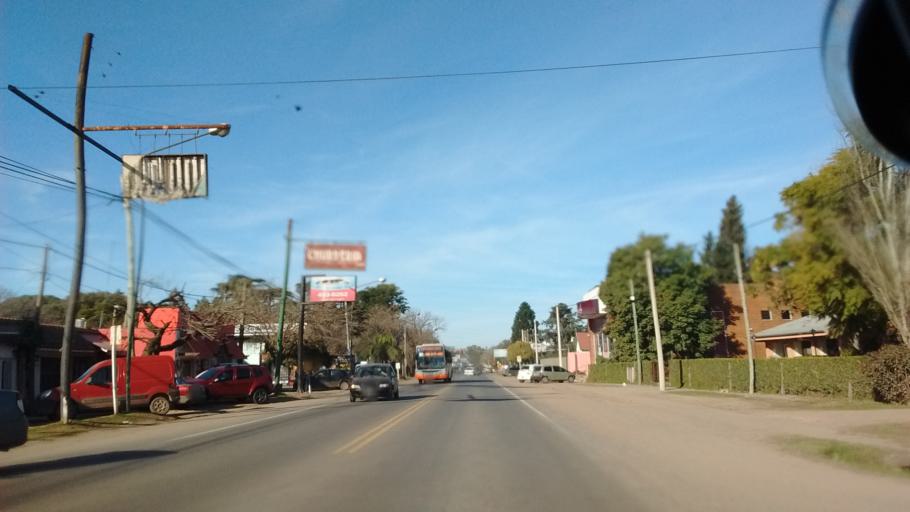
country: AR
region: Santa Fe
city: Funes
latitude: -32.9211
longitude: -60.8135
